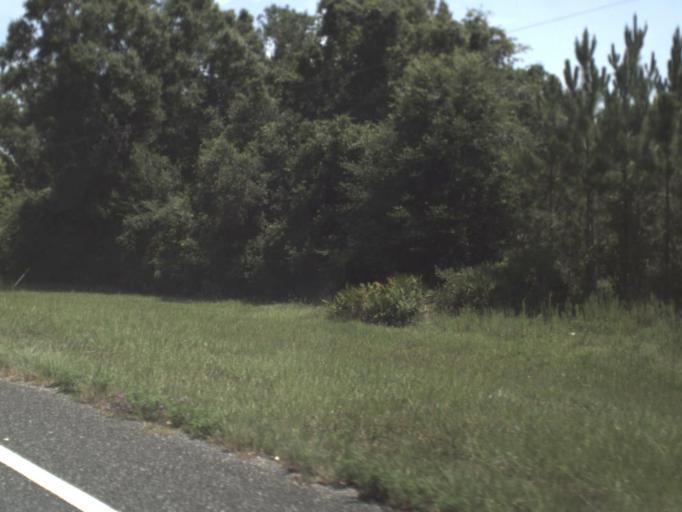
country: US
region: Florida
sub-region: Taylor County
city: Steinhatchee
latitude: 29.7603
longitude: -83.3221
